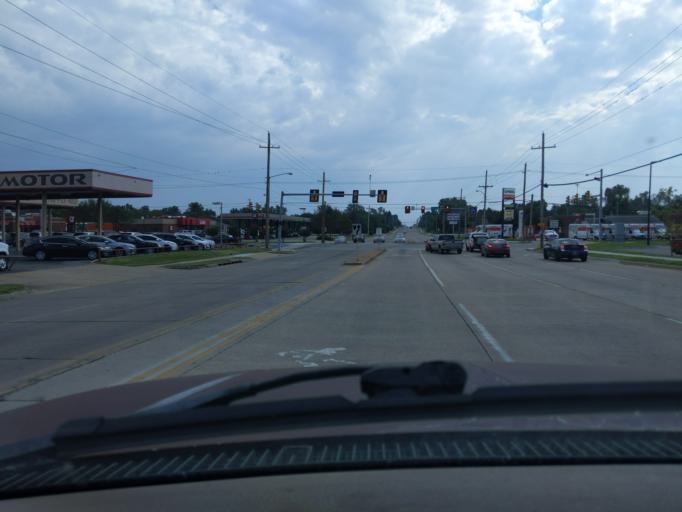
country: US
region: Oklahoma
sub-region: Tulsa County
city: Broken Arrow
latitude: 36.1342
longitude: -95.8333
